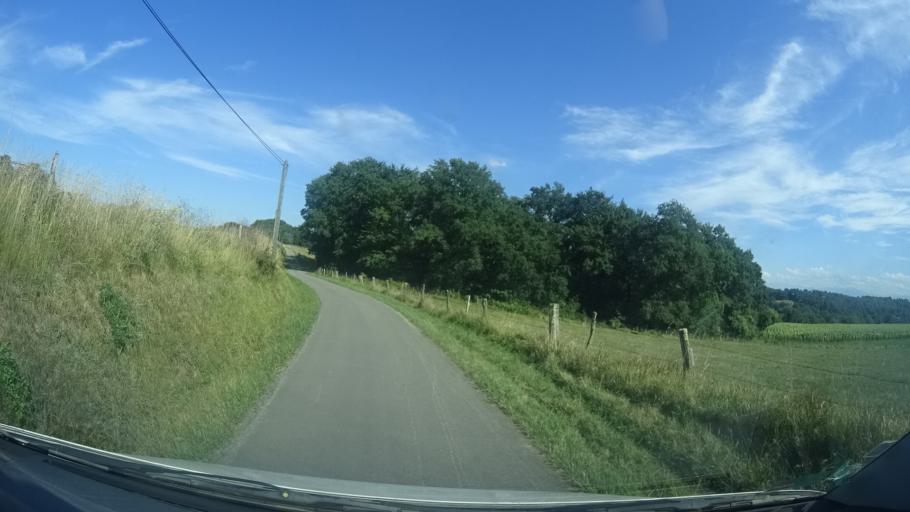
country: FR
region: Aquitaine
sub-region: Departement des Pyrenees-Atlantiques
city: Orthez
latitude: 43.5070
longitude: -0.7021
